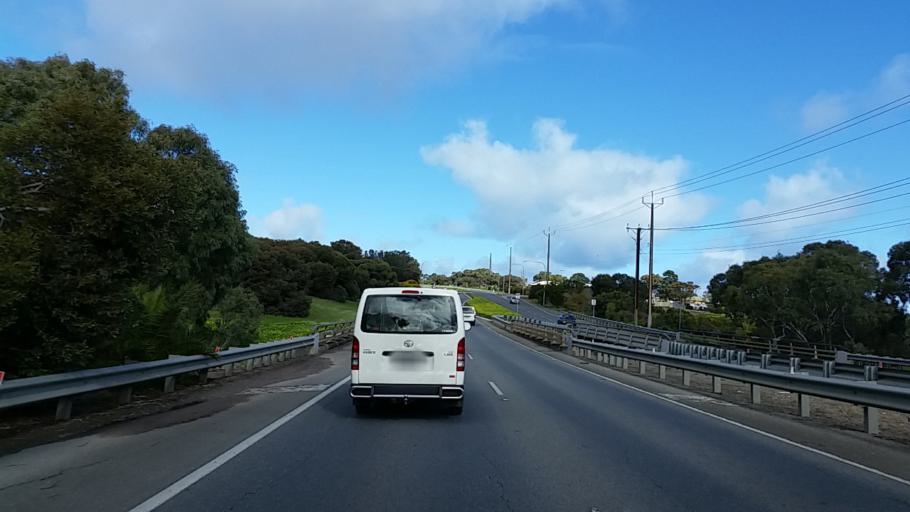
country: AU
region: South Australia
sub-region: Adelaide
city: Port Noarlunga
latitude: -35.1233
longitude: 138.4874
